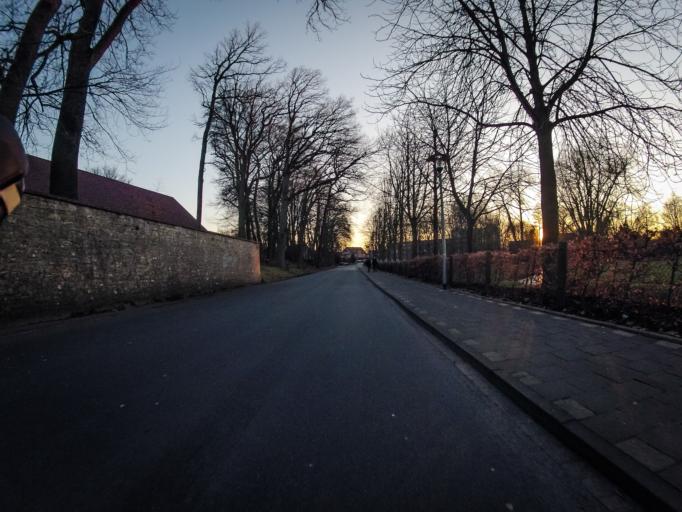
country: DE
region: North Rhine-Westphalia
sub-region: Regierungsbezirk Munster
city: Lotte
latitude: 52.3105
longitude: 7.9438
